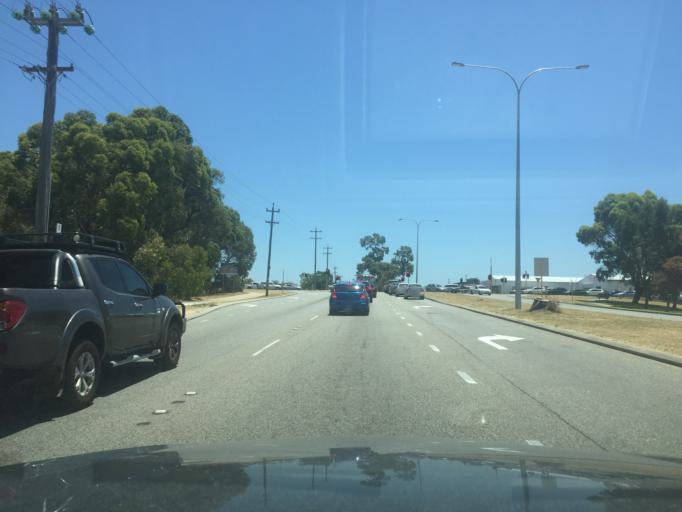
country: AU
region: Western Australia
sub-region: Fremantle
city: Samson
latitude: -32.0642
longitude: 115.7950
